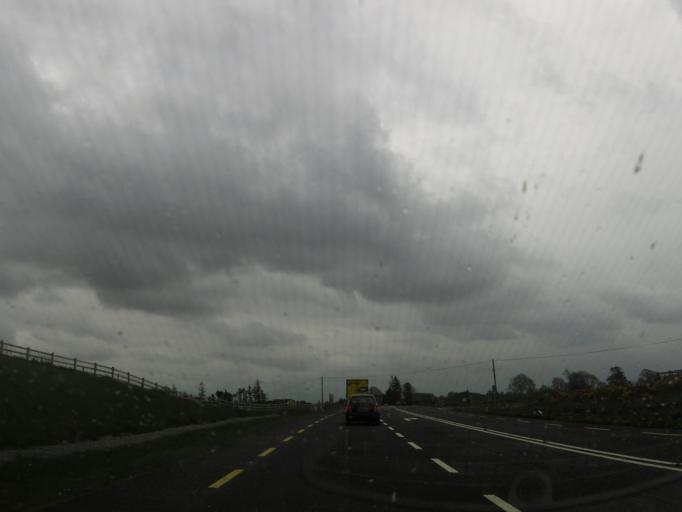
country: IE
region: Connaught
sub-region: County Galway
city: Tuam
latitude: 53.5710
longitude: -8.8411
